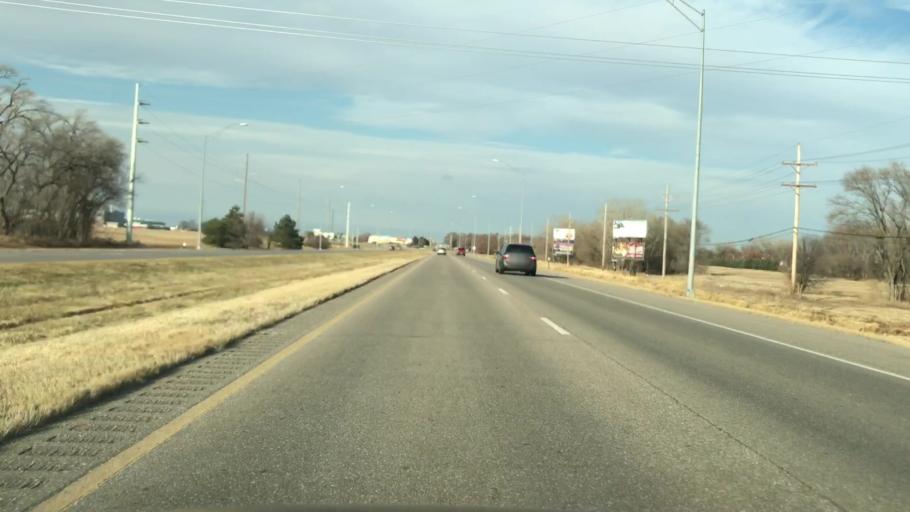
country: US
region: Nebraska
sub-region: Hall County
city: Grand Island
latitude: 40.8915
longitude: -98.3783
